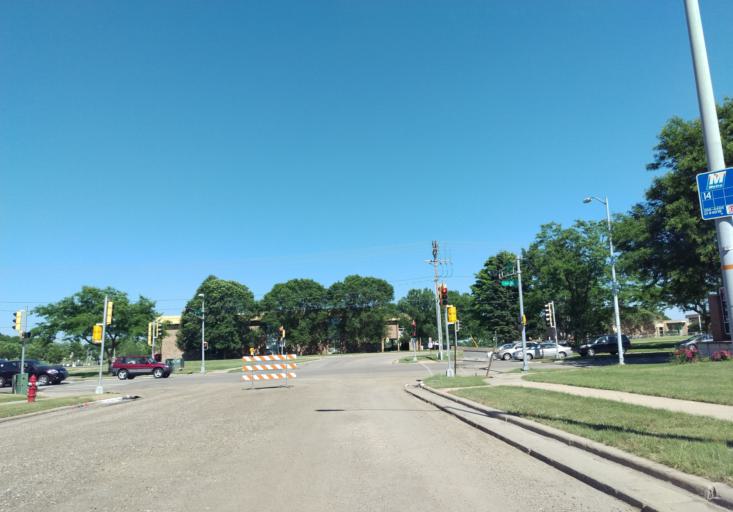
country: US
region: Wisconsin
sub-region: Dane County
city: Middleton
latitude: 43.0656
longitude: -89.5032
